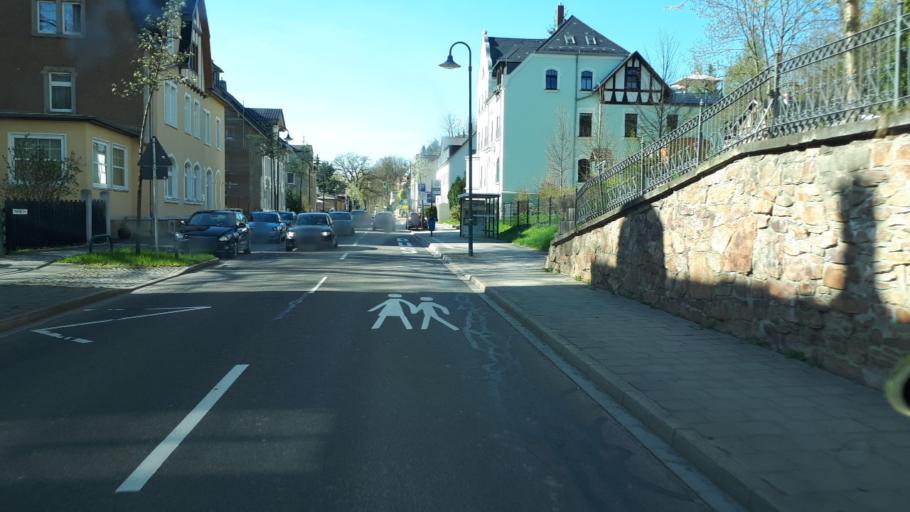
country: DE
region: Saxony
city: Chemnitz
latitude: 50.7868
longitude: 12.9518
